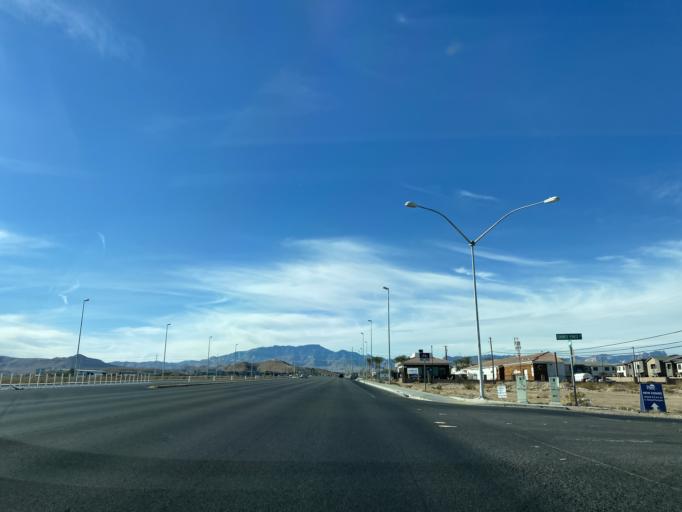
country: US
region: Nevada
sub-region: Clark County
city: Enterprise
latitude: 36.0242
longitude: -115.2342
